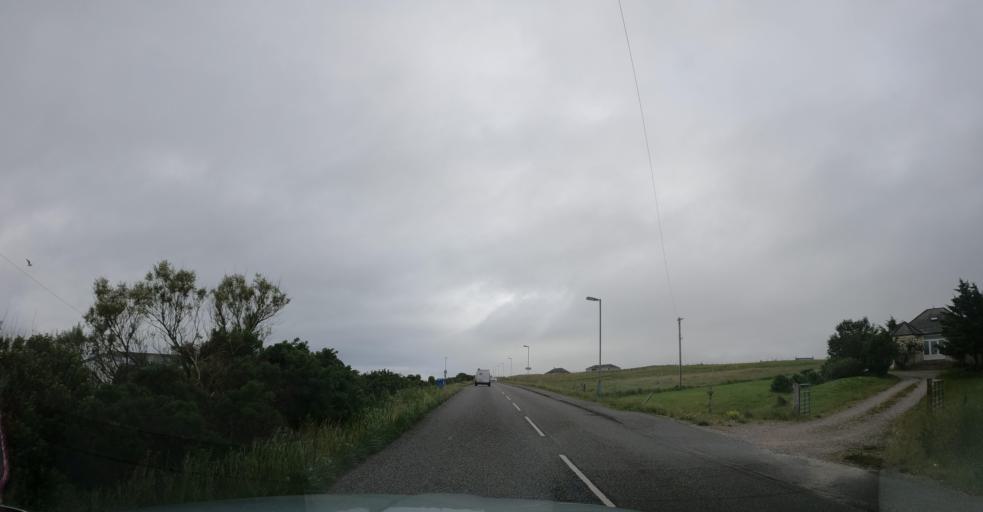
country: GB
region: Scotland
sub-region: Eilean Siar
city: Stornoway
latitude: 58.2060
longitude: -6.2698
